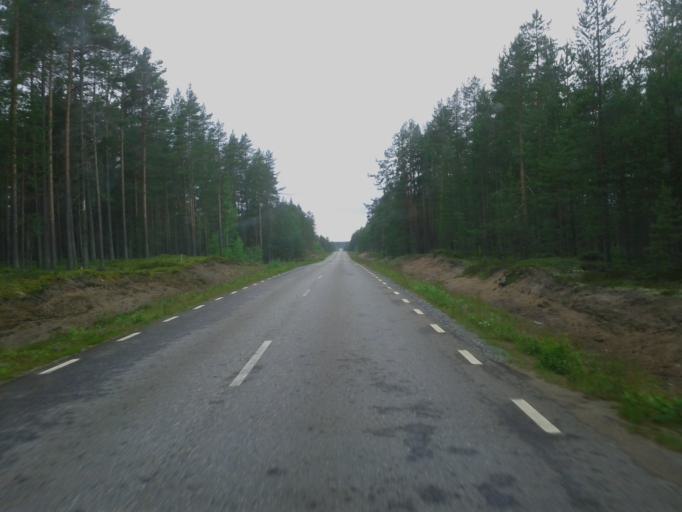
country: SE
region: Vaesterbotten
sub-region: Skelleftea Kommun
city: Kage
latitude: 64.9192
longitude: 20.9431
